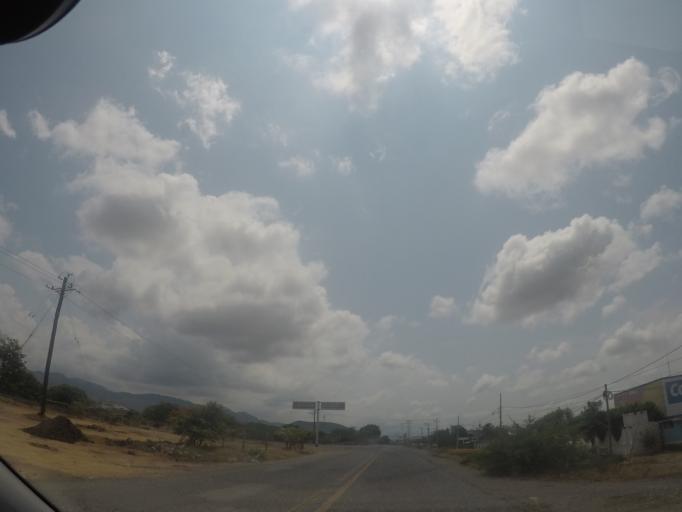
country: MX
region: Oaxaca
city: El Espinal
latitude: 16.5489
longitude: -94.9477
